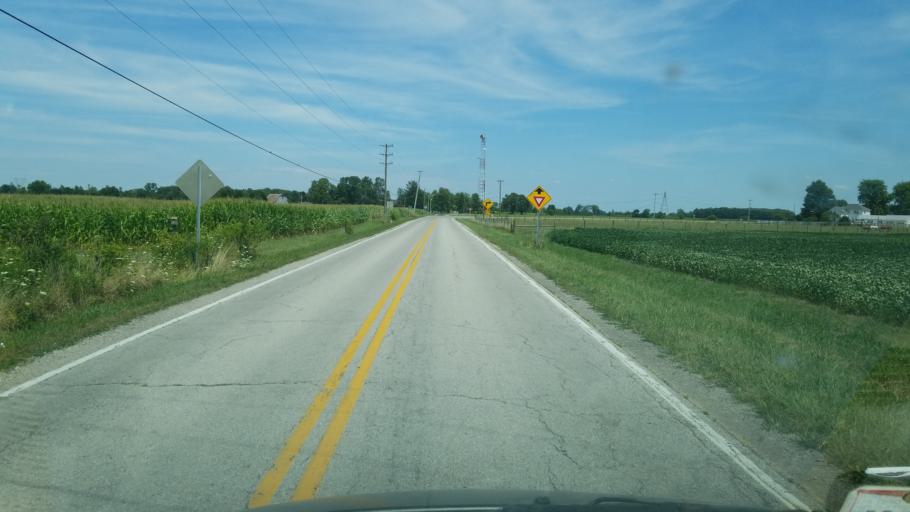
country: US
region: Ohio
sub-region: Madison County
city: West Jefferson
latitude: 39.8811
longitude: -83.3271
